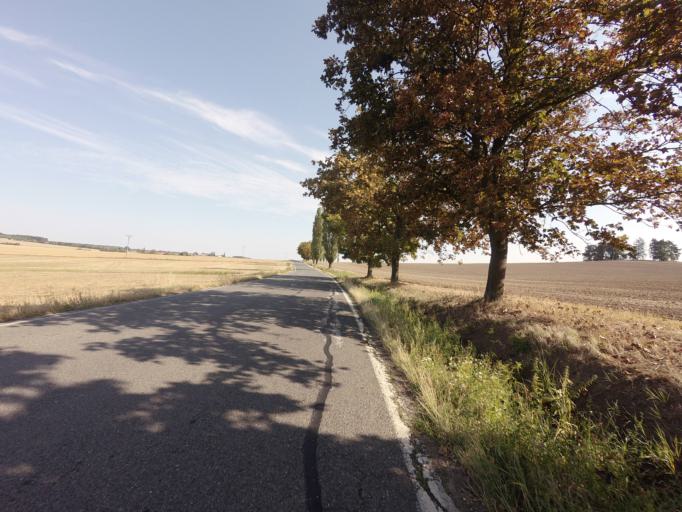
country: CZ
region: Jihocesky
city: Bernartice
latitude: 49.3287
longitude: 14.3597
